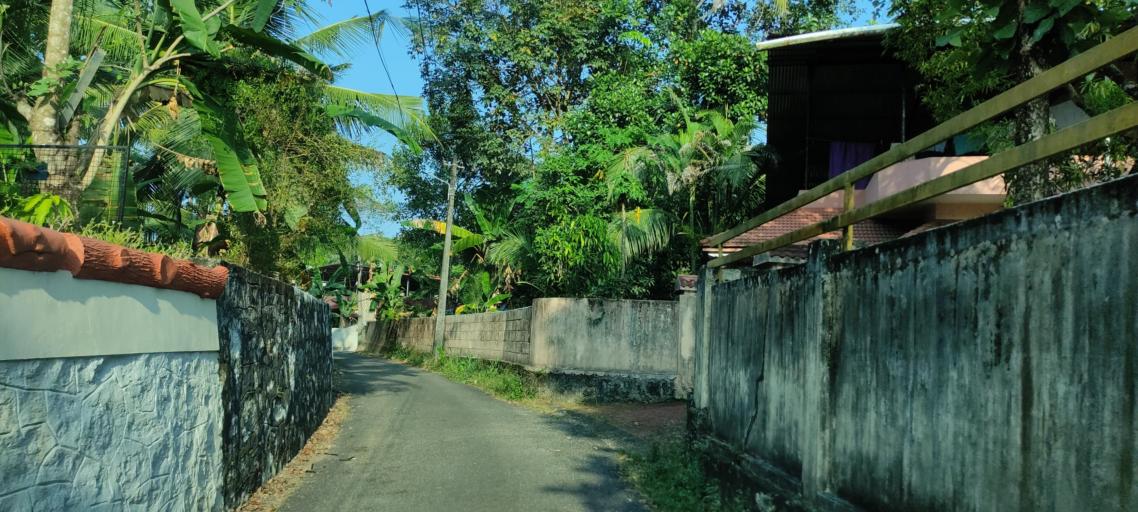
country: IN
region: Kerala
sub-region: Pattanamtitta
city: Adur
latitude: 9.1549
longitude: 76.7401
